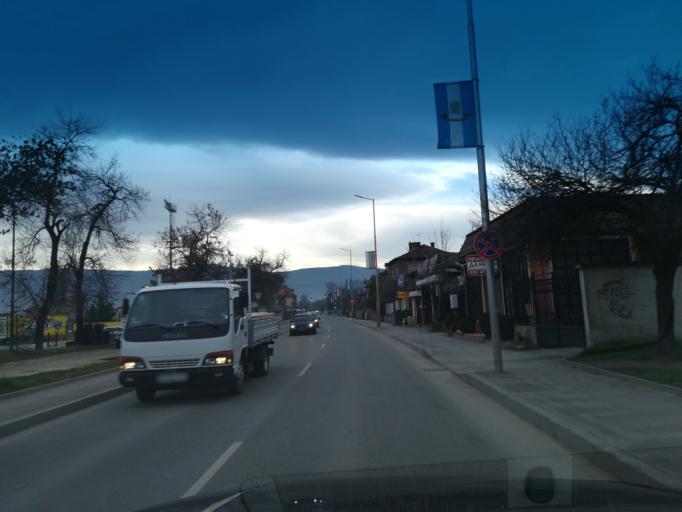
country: BG
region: Plovdiv
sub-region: Obshtina Plovdiv
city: Plovdiv
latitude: 42.1082
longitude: 24.7065
